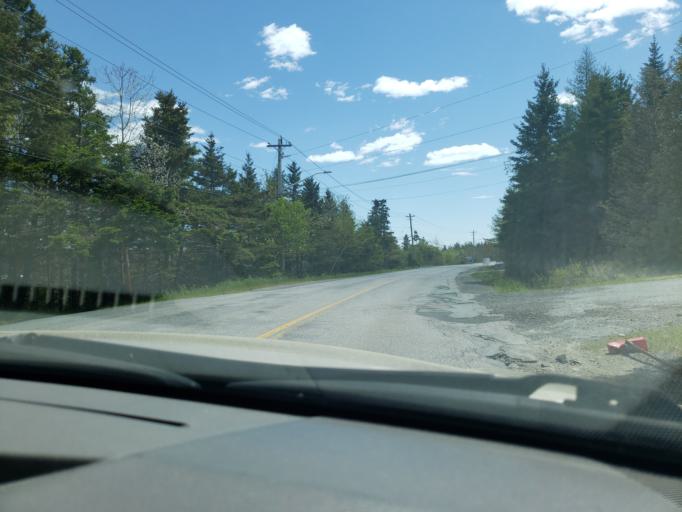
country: CA
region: Nova Scotia
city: Cole Harbour
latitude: 44.7306
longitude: -63.3073
